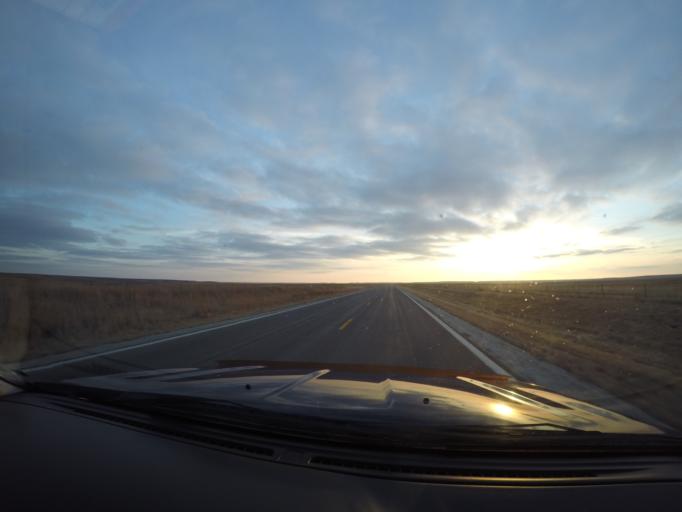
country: US
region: Kansas
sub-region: Chase County
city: Cottonwood Falls
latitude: 38.5120
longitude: -96.5440
